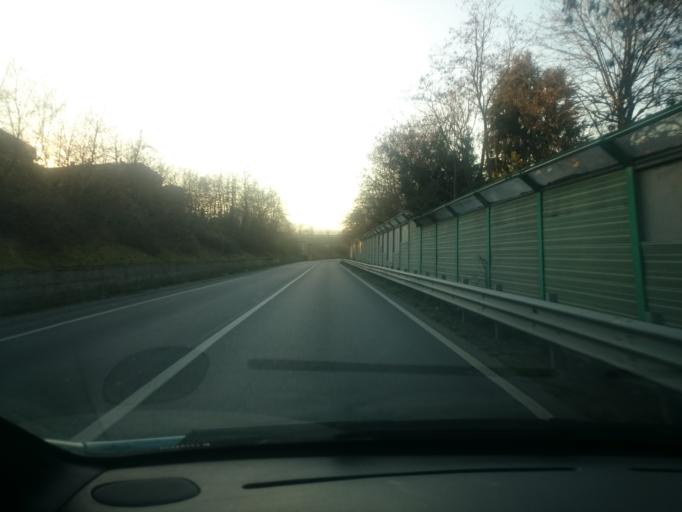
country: IT
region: Emilia-Romagna
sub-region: Provincia di Reggio Emilia
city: Ventoso
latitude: 44.5913
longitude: 10.6888
